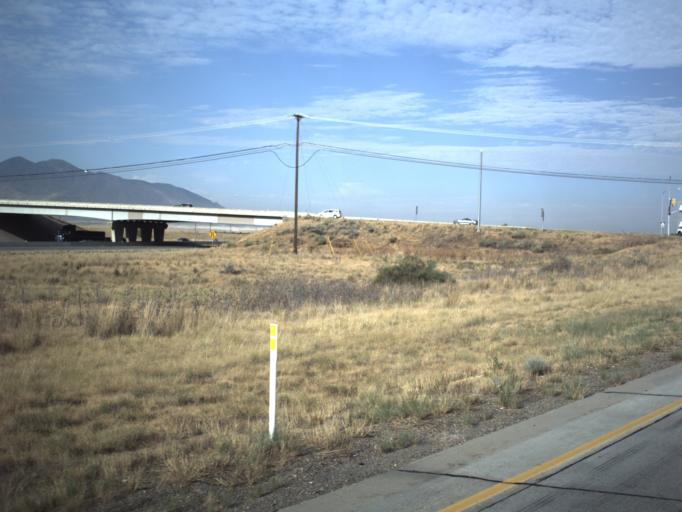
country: US
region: Utah
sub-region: Salt Lake County
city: West Valley City
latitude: 40.7719
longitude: -112.0229
